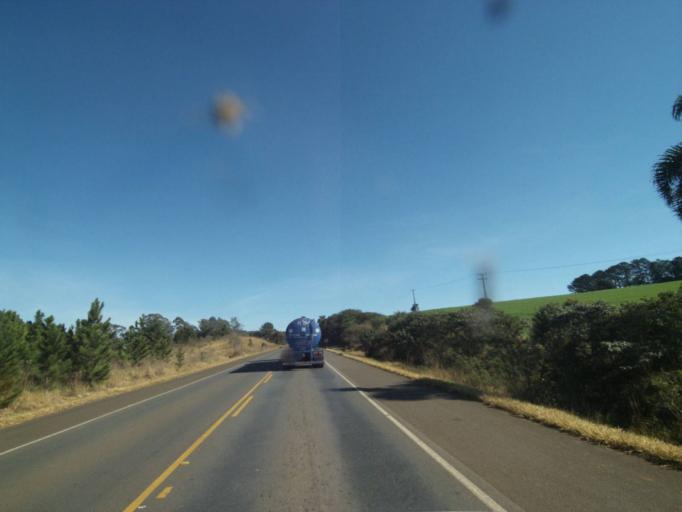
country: BR
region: Parana
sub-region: Tibagi
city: Tibagi
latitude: -24.4910
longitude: -50.4403
